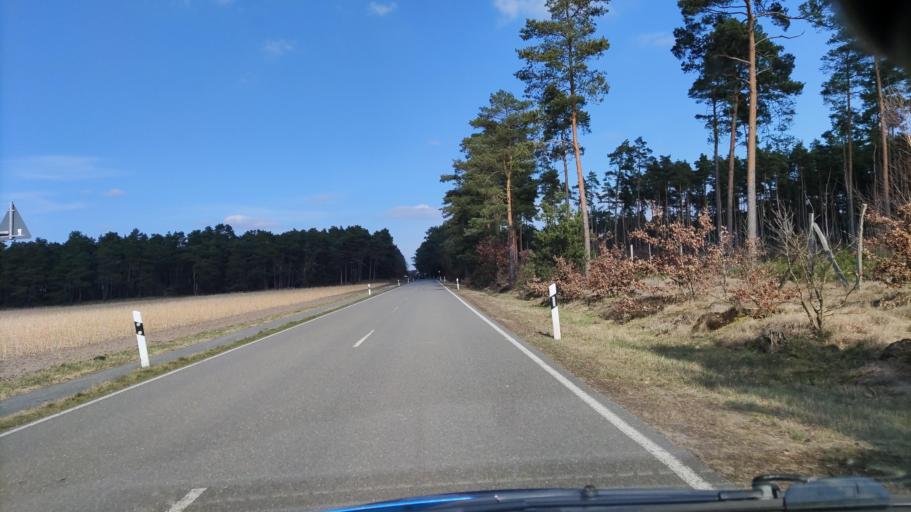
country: DE
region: Lower Saxony
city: Gorleben
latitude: 53.0422
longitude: 11.3497
